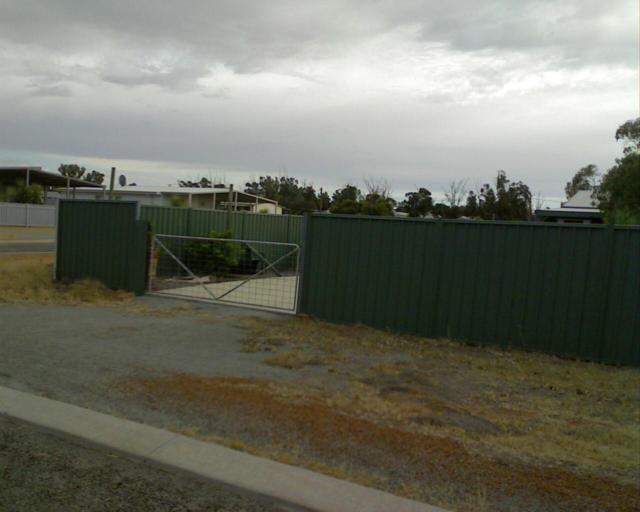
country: AU
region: Western Australia
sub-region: Moora
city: Moora
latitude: -29.8827
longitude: 116.0181
